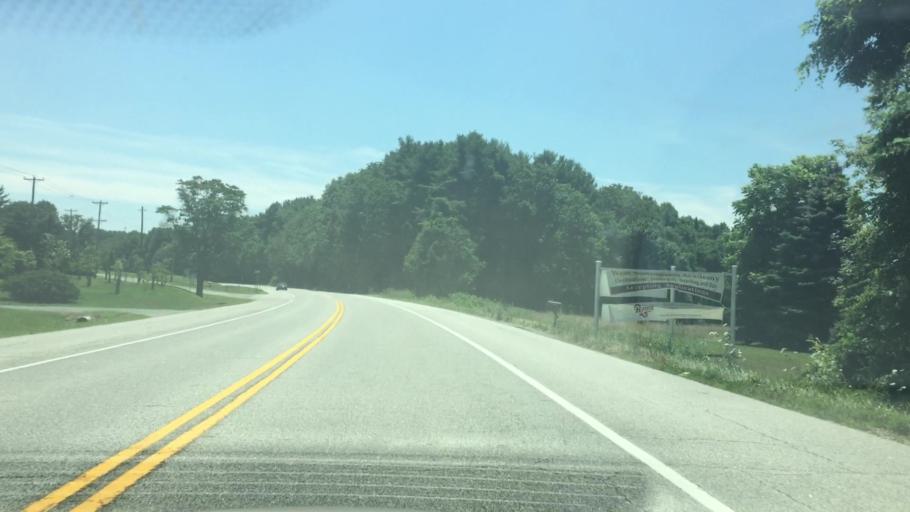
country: US
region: Maryland
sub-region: Cecil County
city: Rising Sun
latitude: 39.6669
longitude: -76.0754
